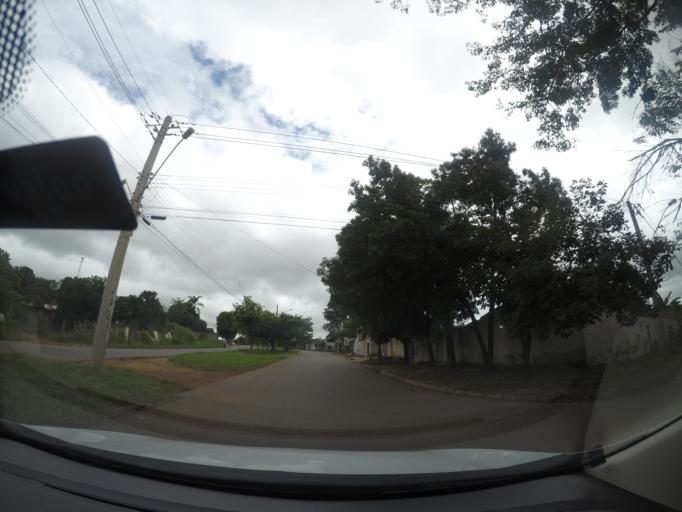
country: BR
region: Goias
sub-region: Goiania
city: Goiania
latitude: -16.7225
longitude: -49.3578
